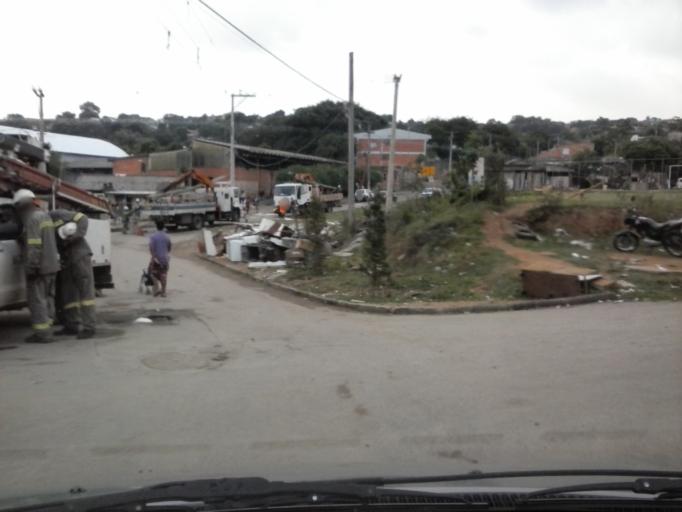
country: BR
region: Rio Grande do Sul
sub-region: Porto Alegre
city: Porto Alegre
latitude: -30.0497
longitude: -51.1568
